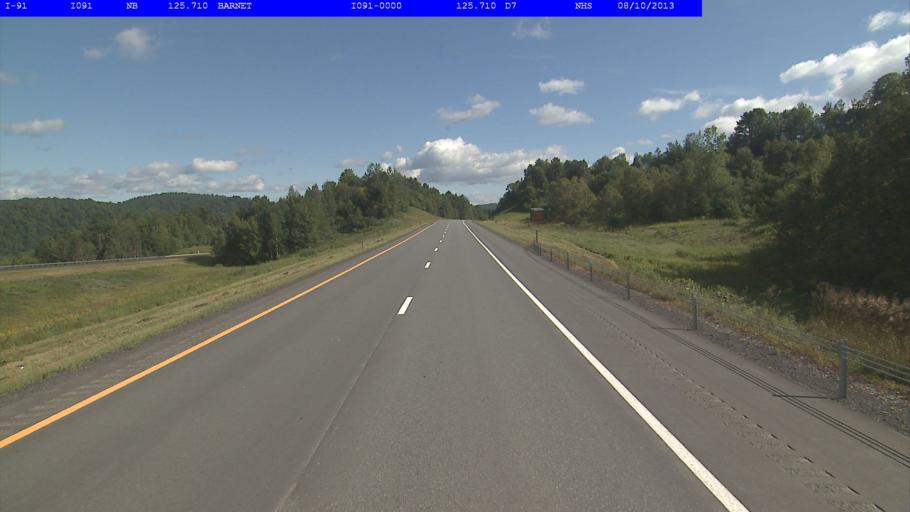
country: US
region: Vermont
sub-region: Caledonia County
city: Saint Johnsbury
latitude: 44.3620
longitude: -72.0310
